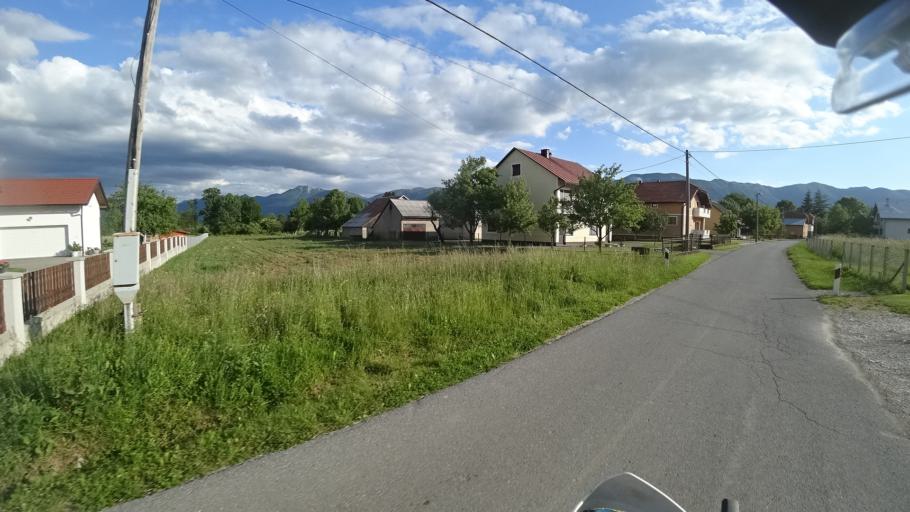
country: HR
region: Licko-Senjska
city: Gospic
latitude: 44.5162
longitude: 15.3320
